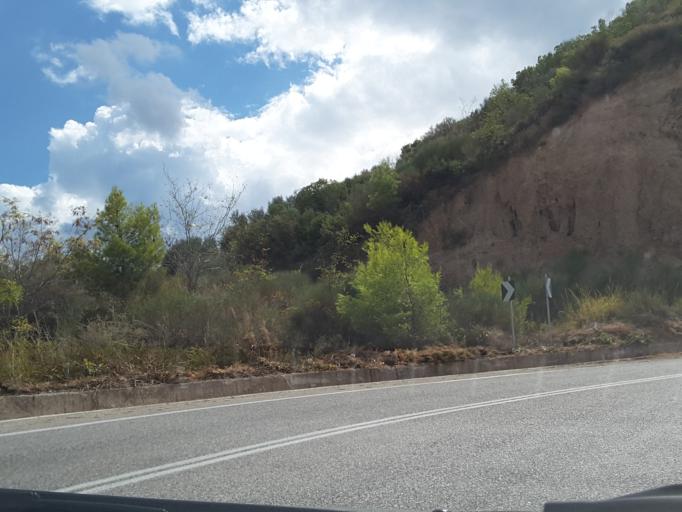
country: GR
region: West Greece
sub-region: Nomos Achaias
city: Akrata
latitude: 38.1438
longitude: 22.2400
